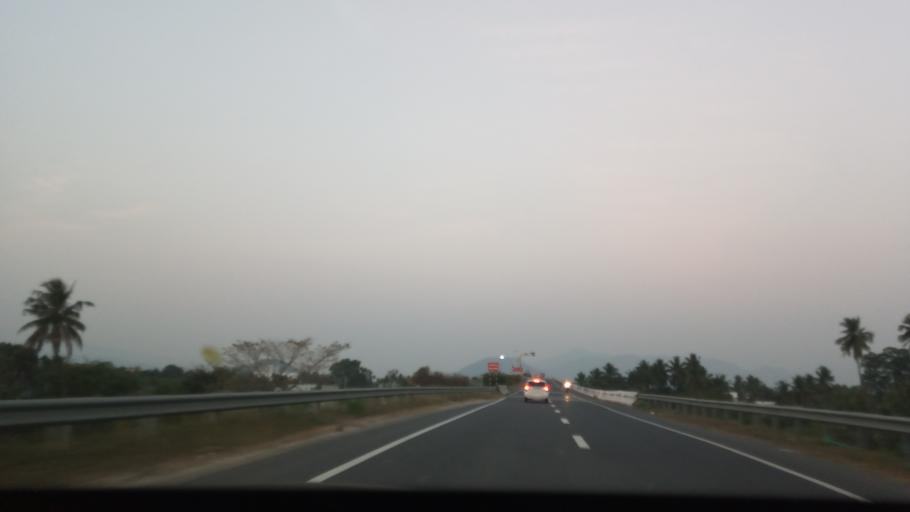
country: IN
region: Tamil Nadu
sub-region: Salem
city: Belur
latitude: 11.6531
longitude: 78.4117
